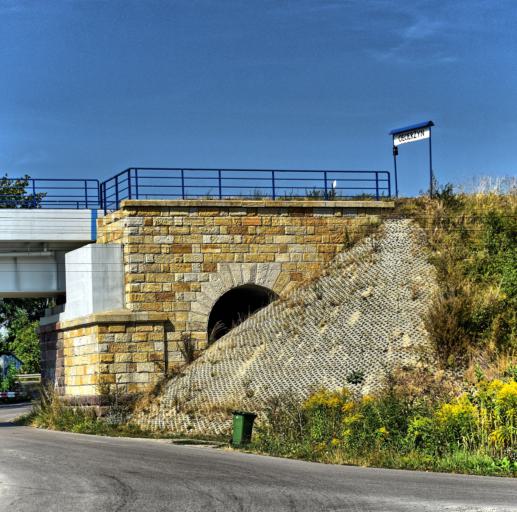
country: PL
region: Lublin Voivodeship
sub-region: Powiat lubelski
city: Niemce
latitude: 51.3183
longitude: 22.6085
